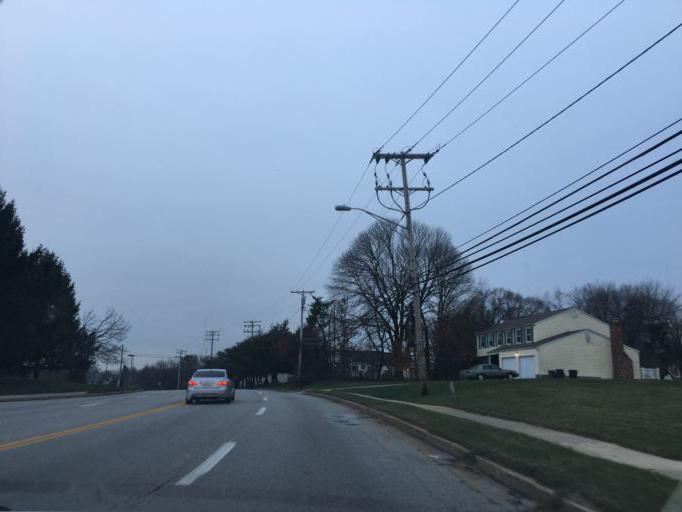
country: US
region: Maryland
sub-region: Baltimore County
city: Woodlawn
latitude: 39.3054
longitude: -76.7546
